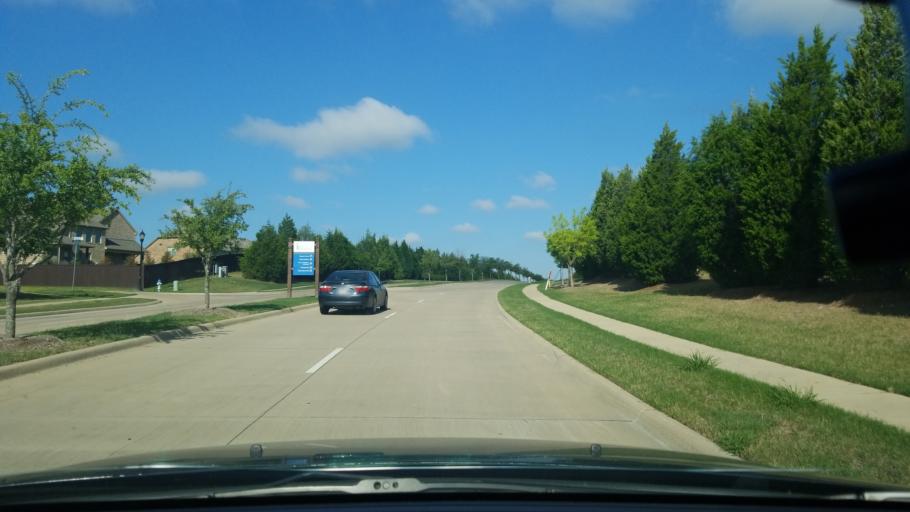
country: US
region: Texas
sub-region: Dallas County
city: Sunnyvale
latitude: 32.8063
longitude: -96.5657
